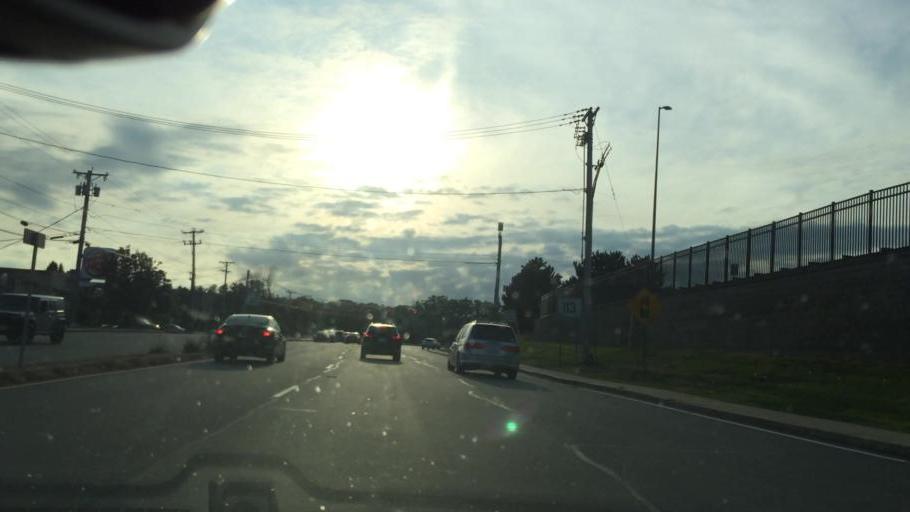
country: US
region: Massachusetts
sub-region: Essex County
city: Lawrence
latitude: 42.7428
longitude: -71.1544
